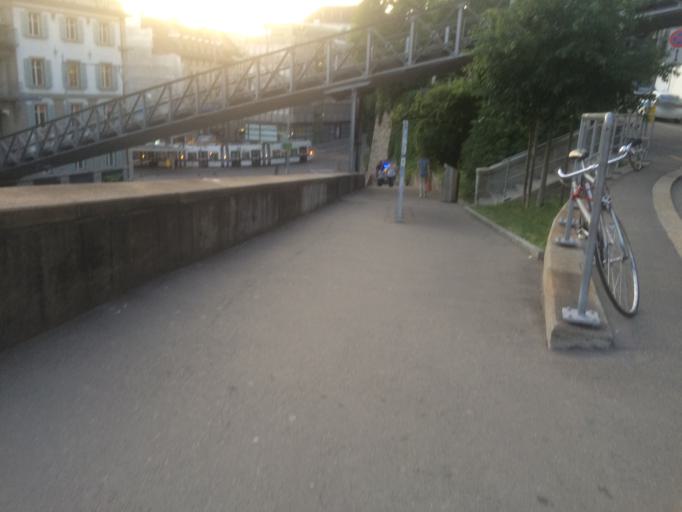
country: CH
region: Zurich
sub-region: Bezirk Zuerich
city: Zuerich (Kreis 1) / Rathaus
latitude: 47.3763
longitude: 8.5450
